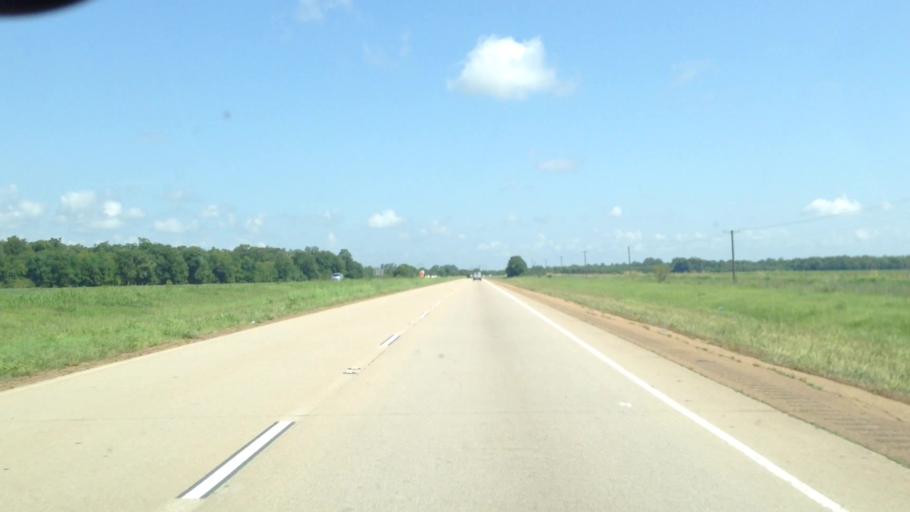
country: US
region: Louisiana
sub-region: Rapides Parish
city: Woodworth
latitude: 31.1785
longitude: -92.4674
